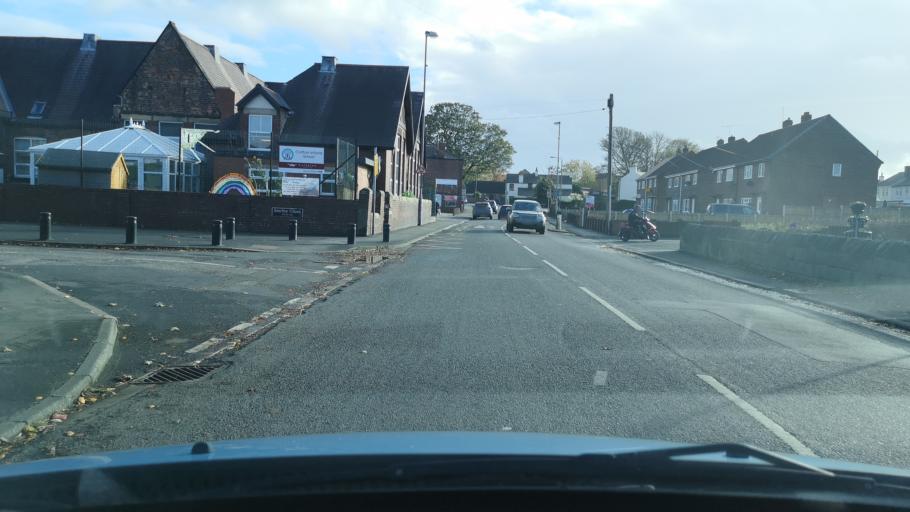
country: GB
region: England
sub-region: City and Borough of Wakefield
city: Crofton
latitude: 53.6556
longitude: -1.4279
